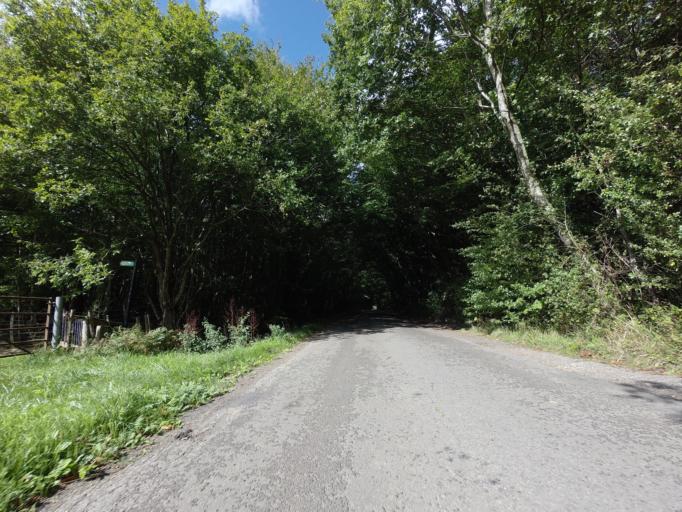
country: GB
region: England
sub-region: Kent
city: Staplehurst
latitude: 51.1338
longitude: 0.5714
